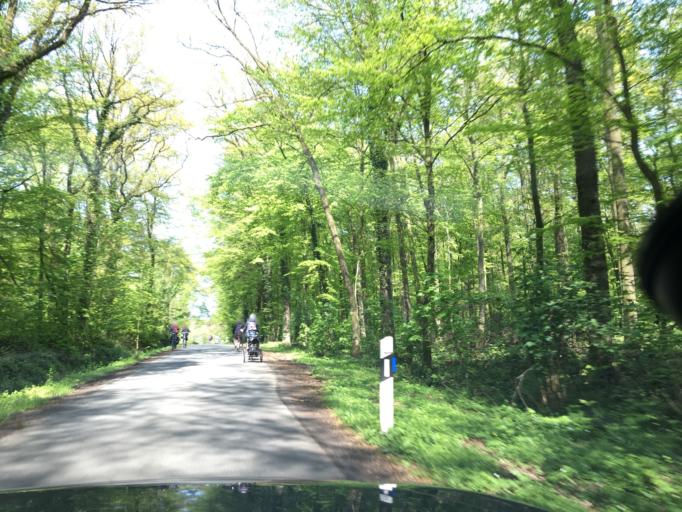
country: DE
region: North Rhine-Westphalia
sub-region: Regierungsbezirk Munster
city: Senden
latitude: 51.8182
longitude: 7.4693
